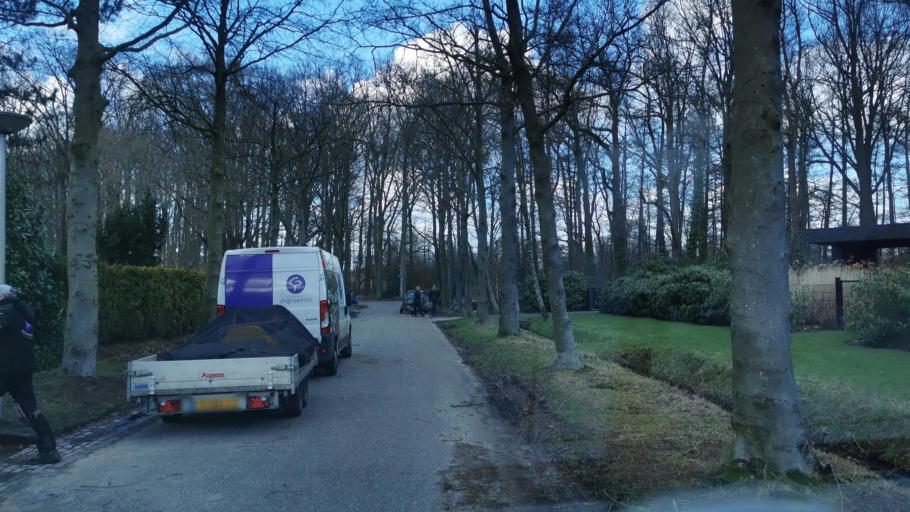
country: NL
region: Overijssel
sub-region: Gemeente Enschede
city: Enschede
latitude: 52.2381
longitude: 6.9250
